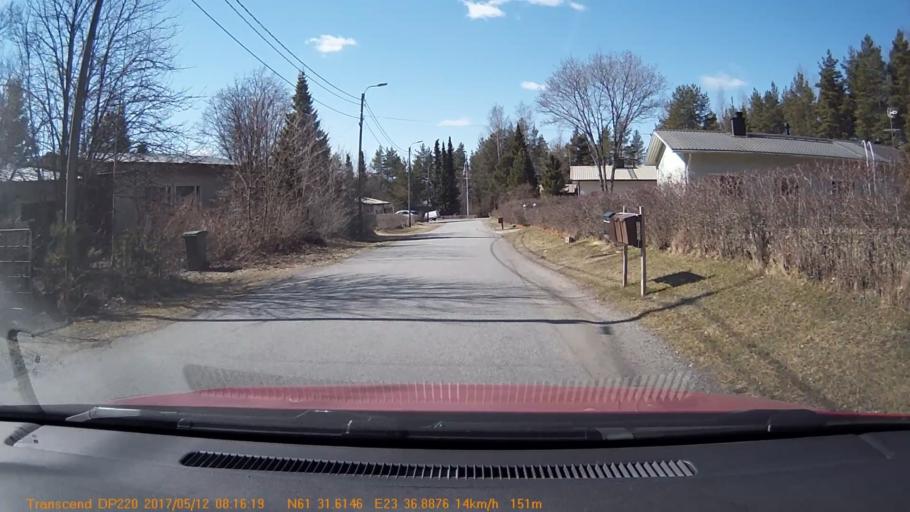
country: FI
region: Pirkanmaa
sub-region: Tampere
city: Yloejaervi
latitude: 61.5270
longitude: 23.6149
